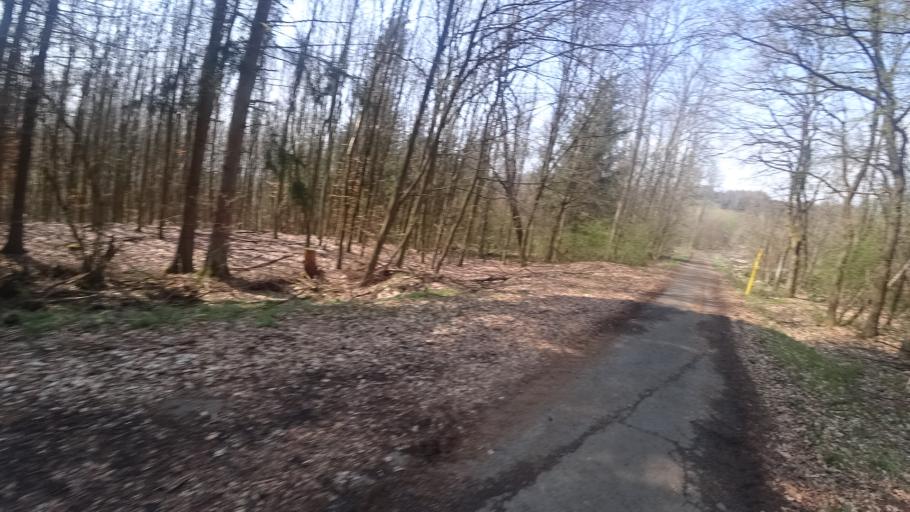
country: DE
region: Rheinland-Pfalz
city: Nauroth
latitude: 50.6985
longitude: 7.8618
